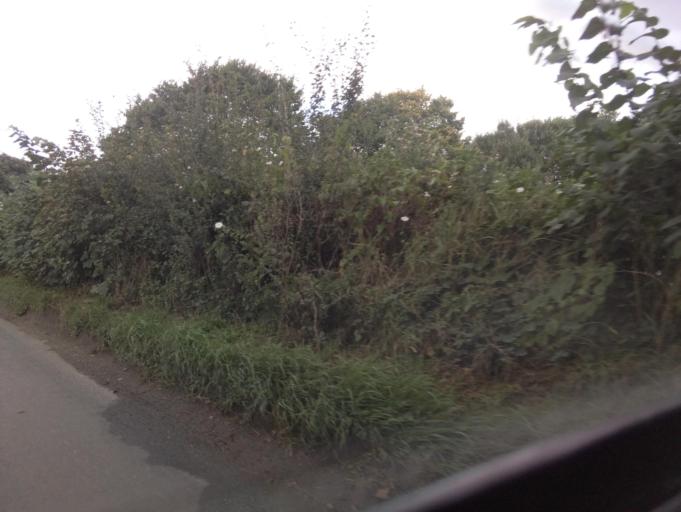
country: GB
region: England
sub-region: North Yorkshire
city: Bedale
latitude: 54.2251
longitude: -1.6622
